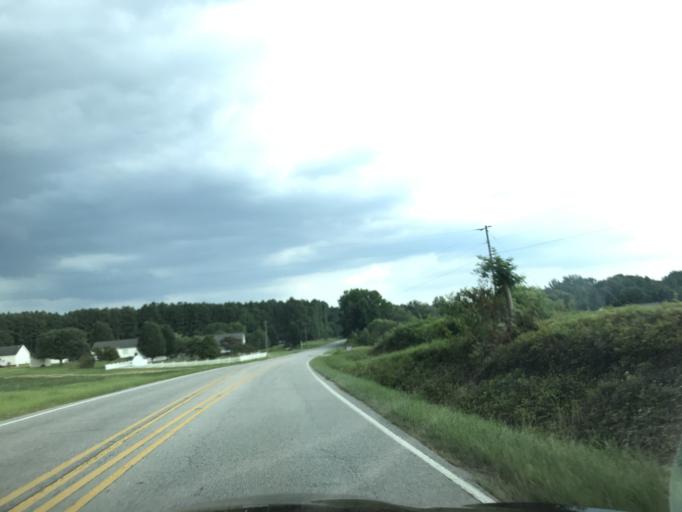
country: US
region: North Carolina
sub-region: Johnston County
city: Four Oaks
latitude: 35.5155
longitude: -78.4978
